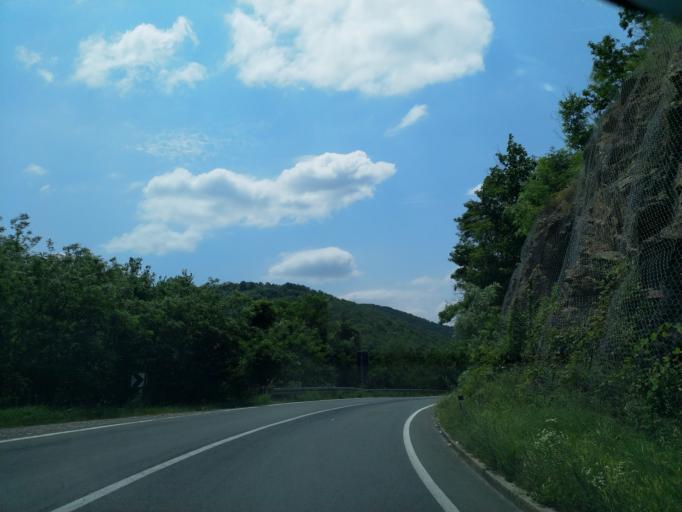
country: RS
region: Central Serbia
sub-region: Rasinski Okrug
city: Aleksandrovac
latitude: 43.4030
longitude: 21.1582
